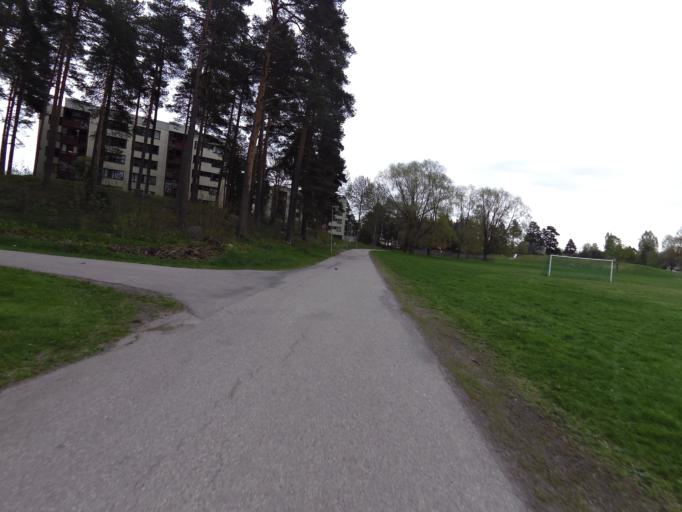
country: SE
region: Gaevleborg
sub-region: Gavle Kommun
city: Gavle
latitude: 60.6879
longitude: 17.1202
